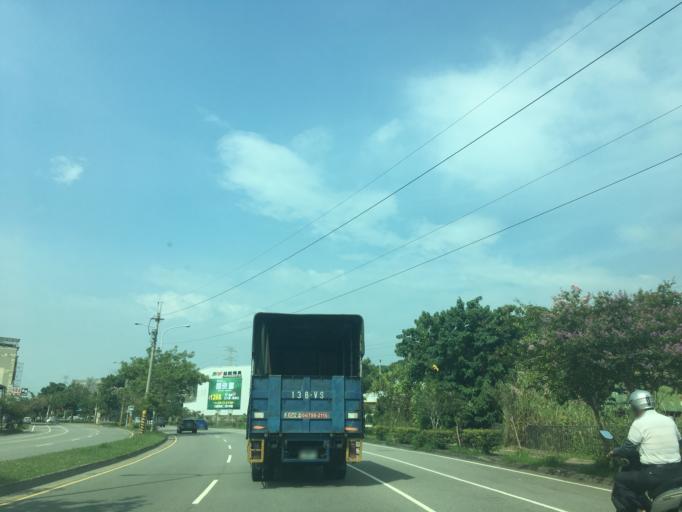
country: TW
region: Taiwan
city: Fengyuan
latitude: 24.2469
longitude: 120.7355
